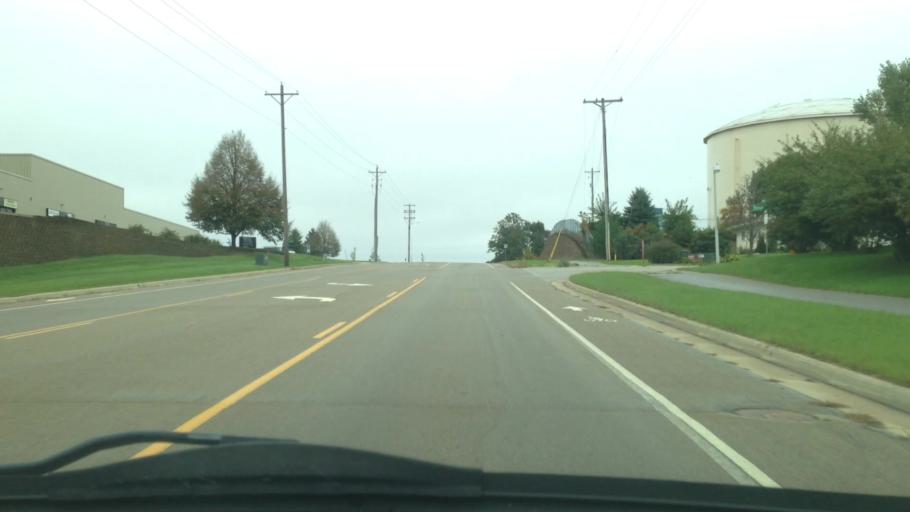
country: US
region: Minnesota
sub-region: Olmsted County
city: Rochester
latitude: 44.0904
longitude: -92.5087
